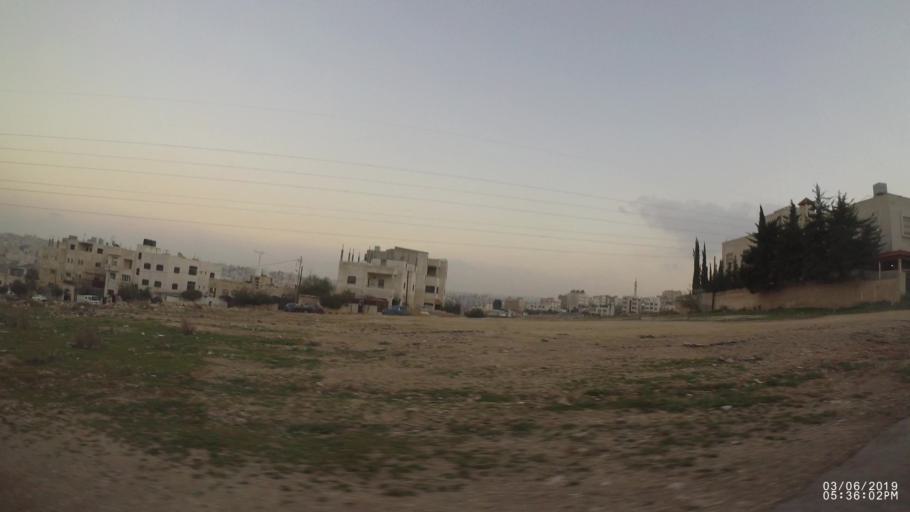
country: JO
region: Amman
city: Amman
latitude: 31.9895
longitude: 35.9721
